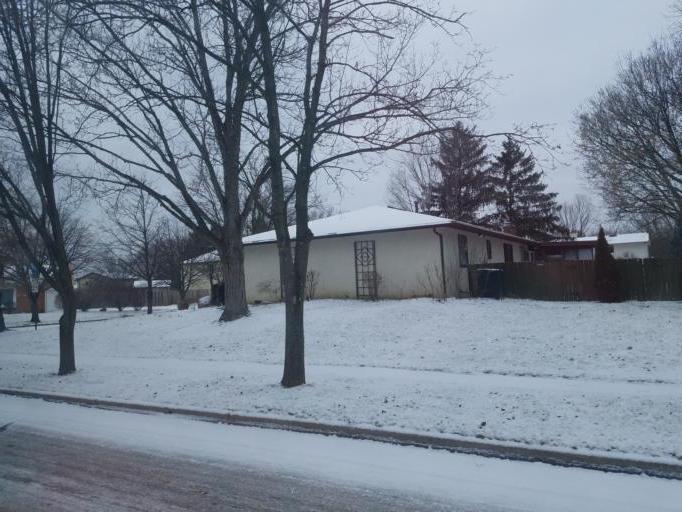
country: US
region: Ohio
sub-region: Delaware County
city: Powell
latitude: 40.1241
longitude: -83.0816
